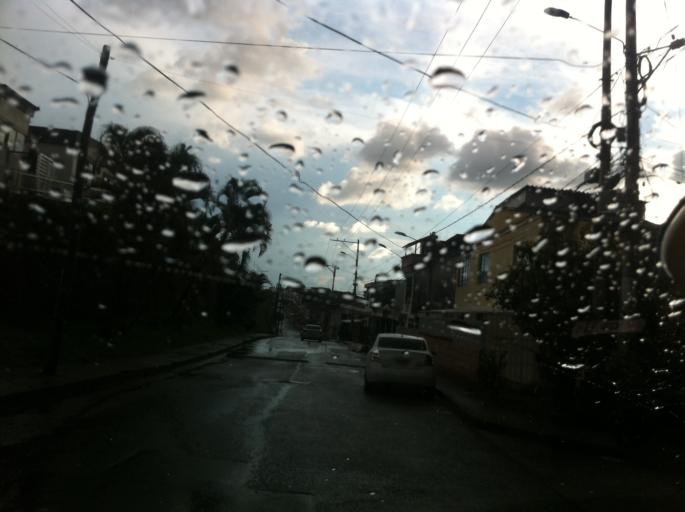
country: CO
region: Quindio
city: Armenia
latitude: 4.5568
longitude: -75.6664
